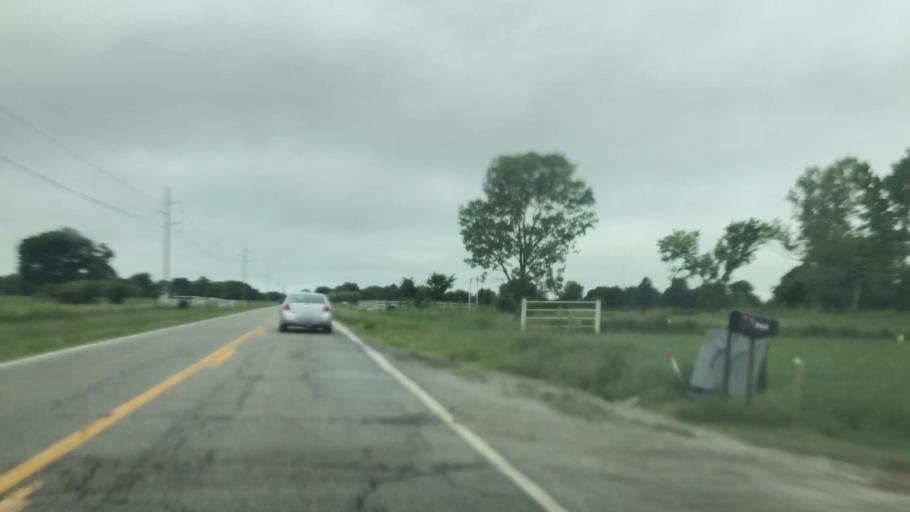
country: US
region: Oklahoma
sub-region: Washington County
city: Dewey
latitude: 36.7280
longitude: -95.8351
